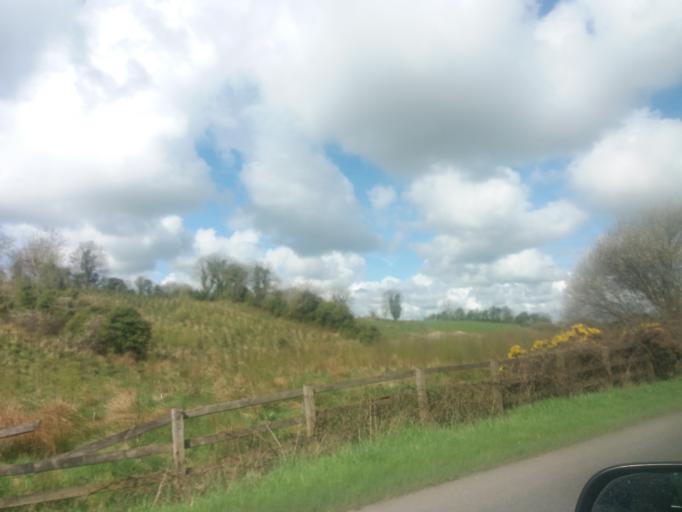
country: IE
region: Ulster
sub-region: An Cabhan
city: Ballyjamesduff
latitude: 53.9171
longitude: -7.2069
